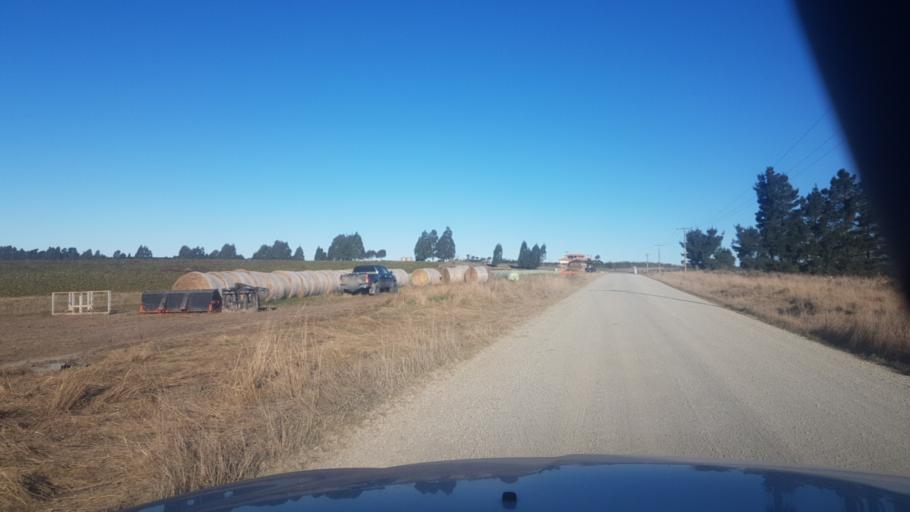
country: NZ
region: Canterbury
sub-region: Timaru District
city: Pleasant Point
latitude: -44.3570
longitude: 171.0692
